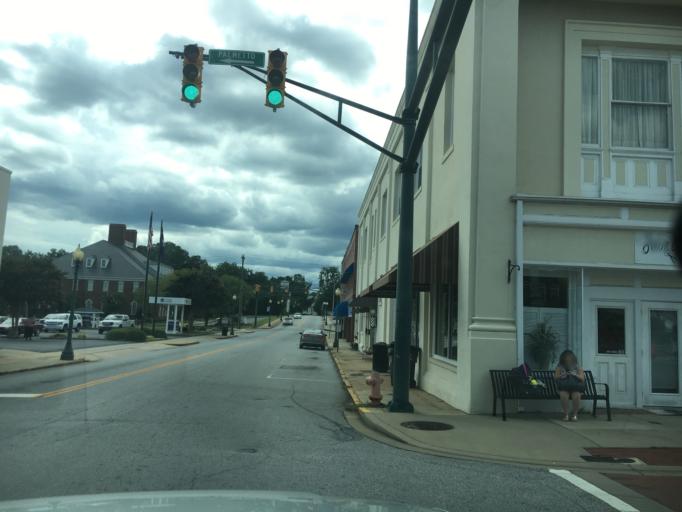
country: US
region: South Carolina
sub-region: Laurens County
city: Laurens
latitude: 34.4989
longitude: -82.0146
